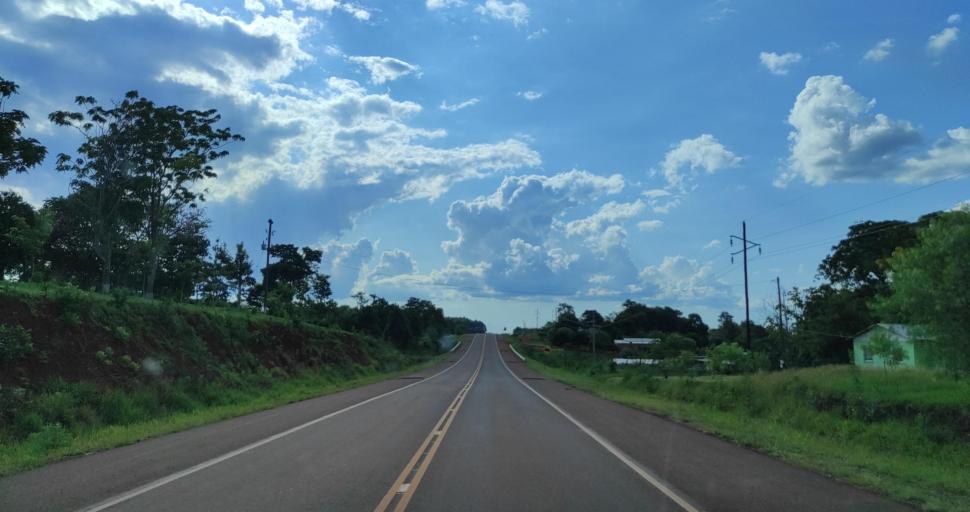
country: AR
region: Misiones
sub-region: Departamento de San Pedro
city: San Pedro
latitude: -26.3730
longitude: -53.9331
